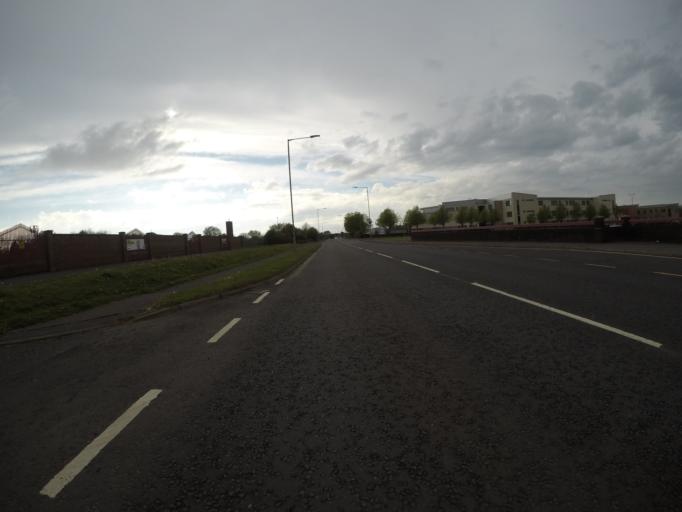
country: GB
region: Scotland
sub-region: North Ayrshire
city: Dreghorn
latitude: 55.6069
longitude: -4.6320
